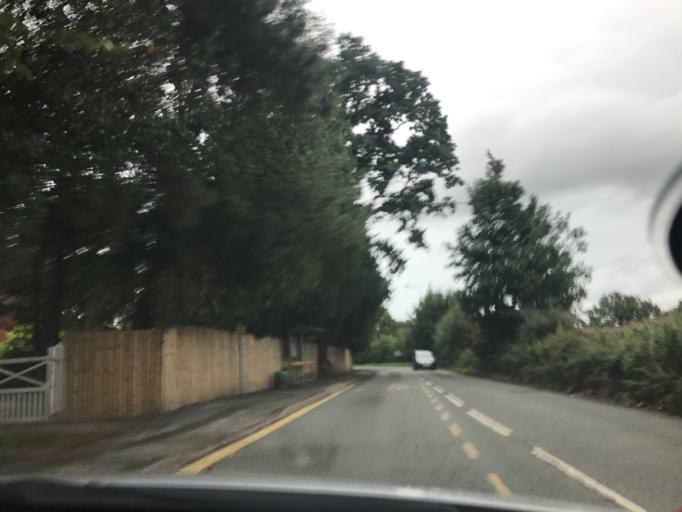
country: GB
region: England
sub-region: Cheshire West and Chester
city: Northwich
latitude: 53.2231
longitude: -2.5110
